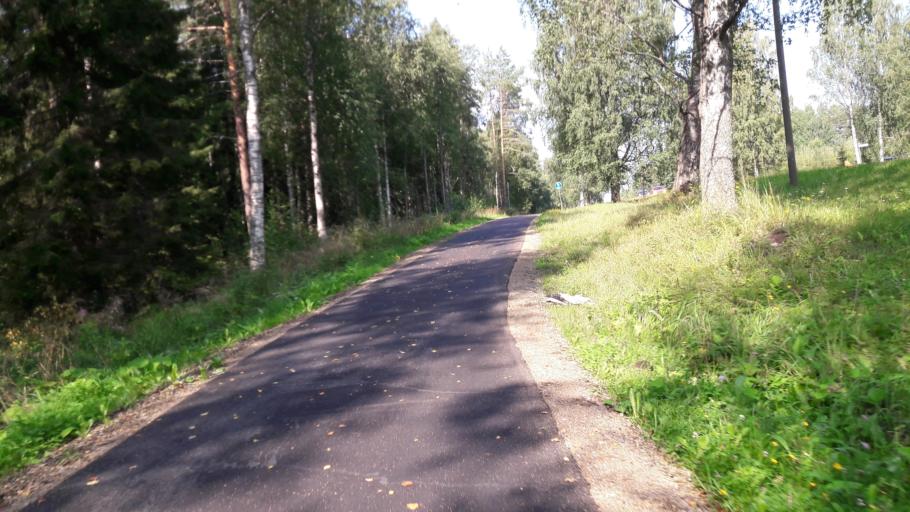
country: FI
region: North Karelia
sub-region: Joensuu
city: Joensuu
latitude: 62.5339
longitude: 29.8492
